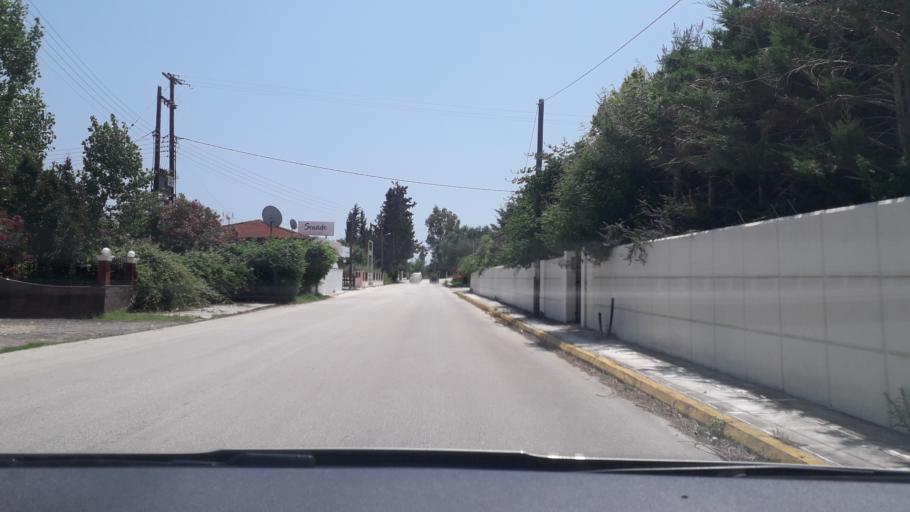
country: GR
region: Ionian Islands
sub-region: Nomos Kerkyras
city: Lefkimmi
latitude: 39.3975
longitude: 20.1016
